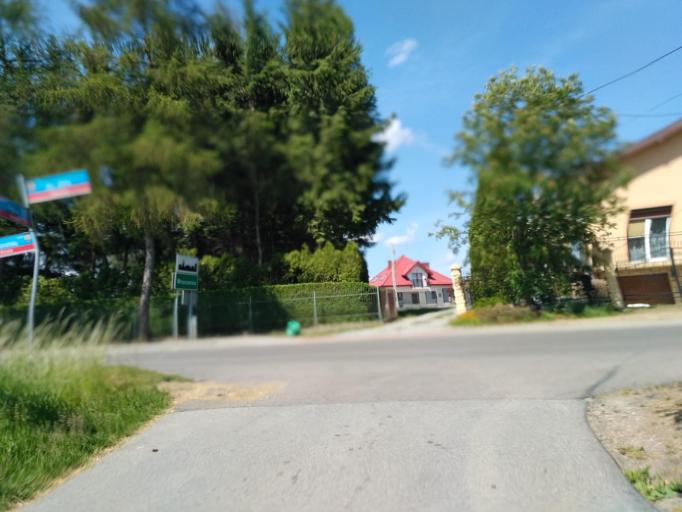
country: PL
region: Subcarpathian Voivodeship
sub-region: Powiat krosnienski
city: Miejsce Piastowe
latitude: 49.6451
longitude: 21.7510
